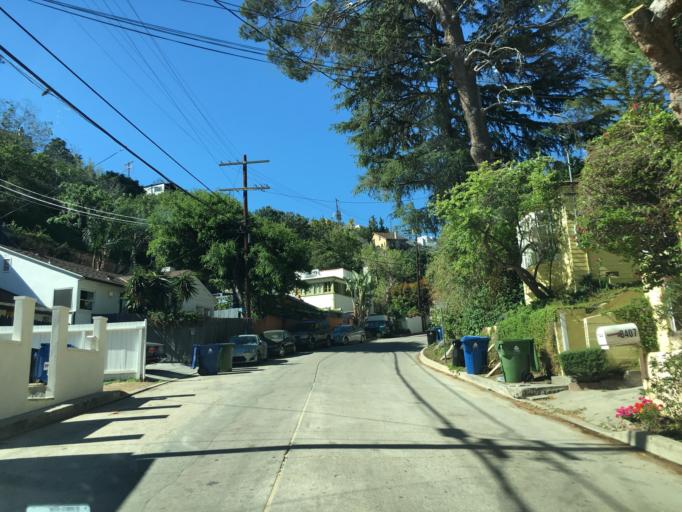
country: US
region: California
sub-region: Los Angeles County
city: West Hollywood
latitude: 34.1039
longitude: -118.3735
